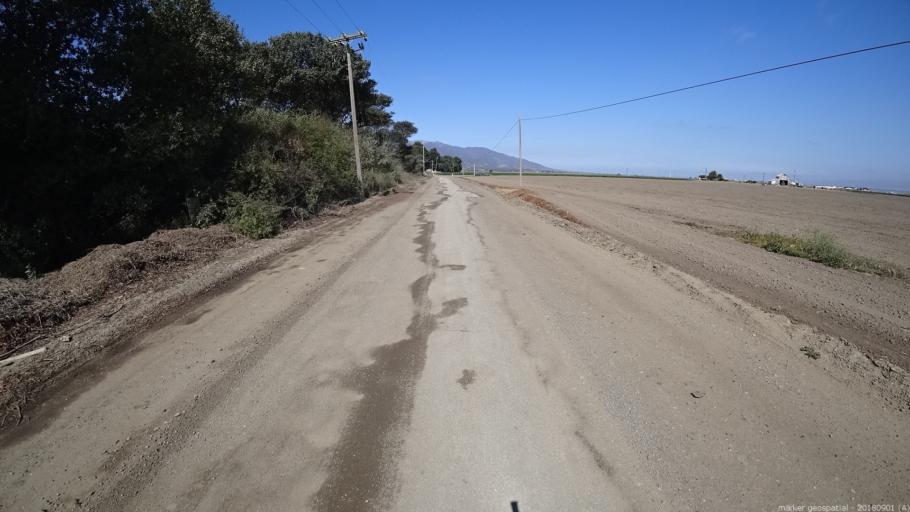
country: US
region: California
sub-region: Monterey County
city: Gonzales
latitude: 36.4886
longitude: -121.4692
